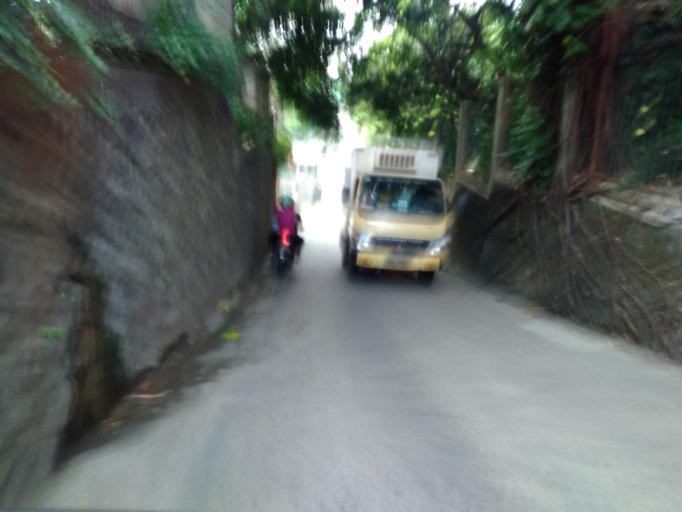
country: ID
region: Jakarta Raya
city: Jakarta
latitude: -6.2728
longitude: 106.8112
